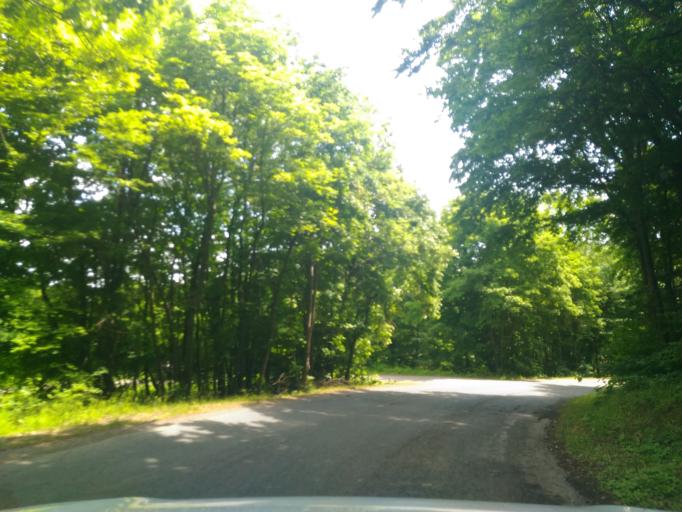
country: HU
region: Baranya
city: Pecs
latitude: 46.1337
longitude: 18.2321
